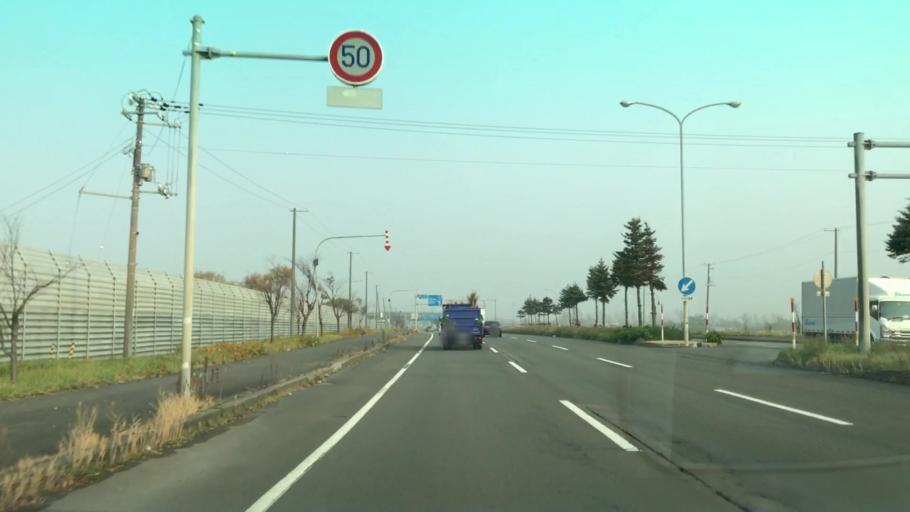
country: JP
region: Hokkaido
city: Ishikari
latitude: 43.1748
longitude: 141.3483
